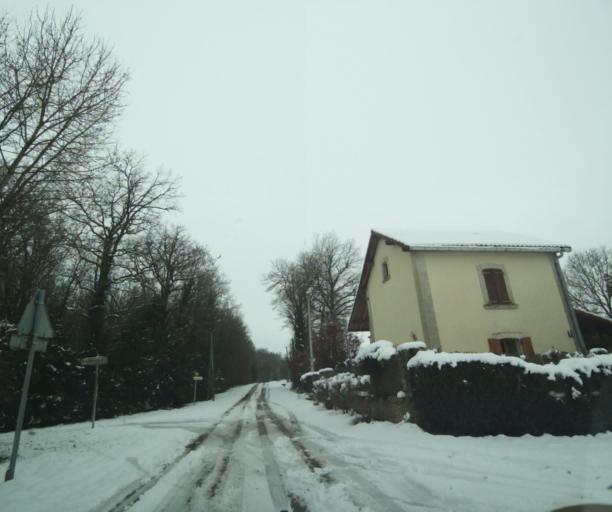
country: FR
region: Champagne-Ardenne
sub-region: Departement de la Haute-Marne
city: Montier-en-Der
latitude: 48.4682
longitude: 4.6574
